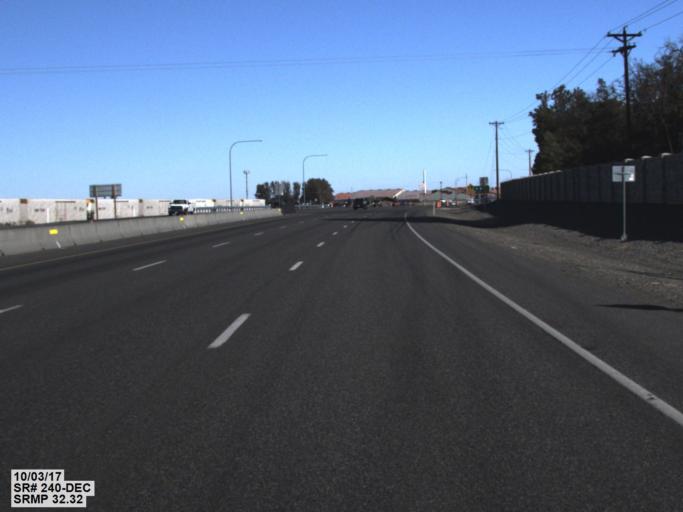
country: US
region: Washington
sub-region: Benton County
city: Richland
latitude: 46.2890
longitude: -119.3062
